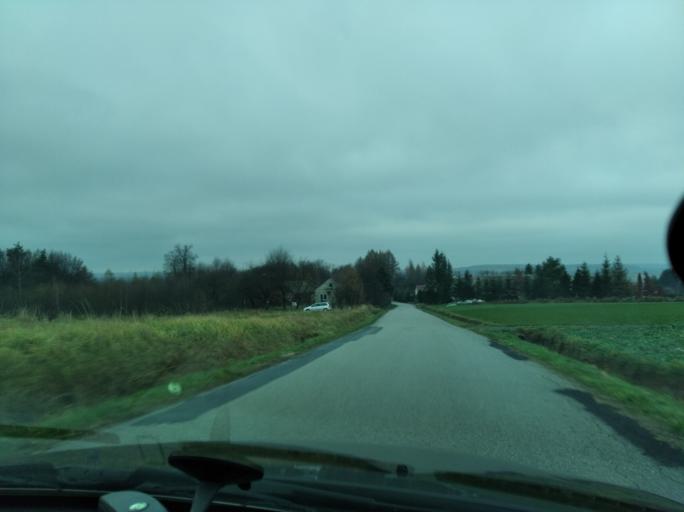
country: PL
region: Subcarpathian Voivodeship
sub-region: Powiat przeworski
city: Jawornik Polski
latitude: 49.8984
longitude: 22.2767
